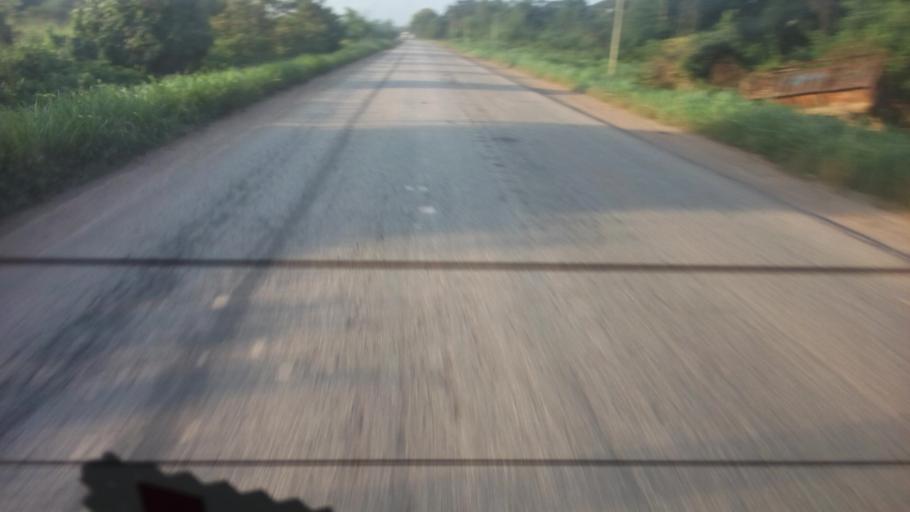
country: GH
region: Western
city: Tarkwa
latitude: 5.1906
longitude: -2.0357
